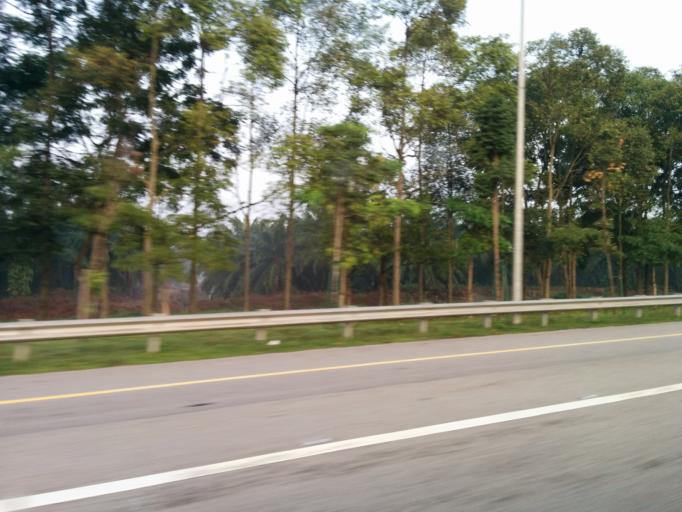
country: MY
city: Sungai Pelek New Village
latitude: 2.7566
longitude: 101.6881
